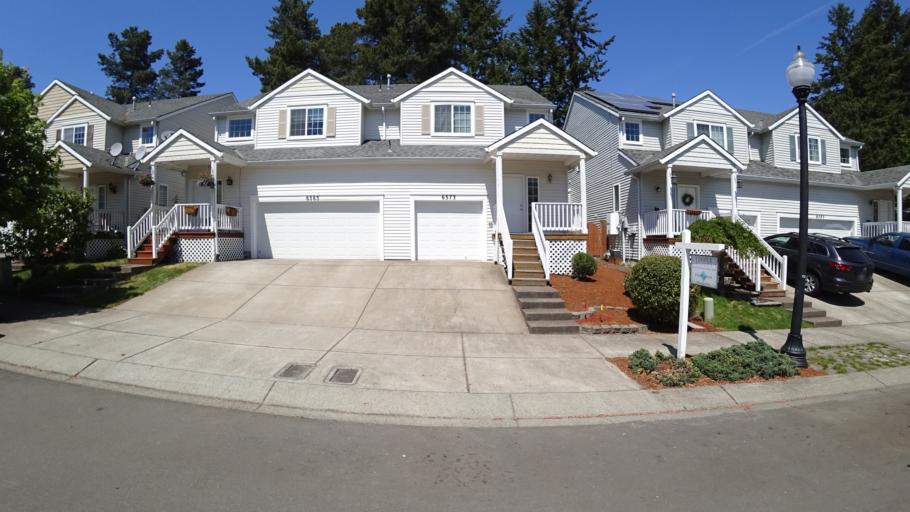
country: US
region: Oregon
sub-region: Washington County
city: Rockcreek
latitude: 45.5221
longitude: -122.9133
